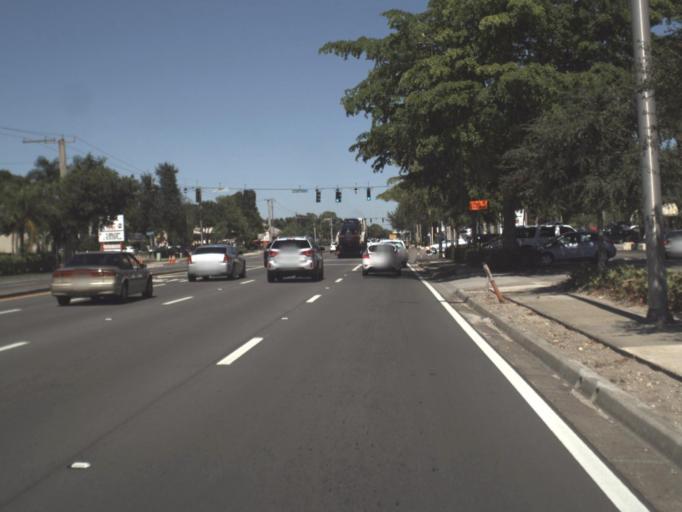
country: US
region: Florida
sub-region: Collier County
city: Naples
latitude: 26.1652
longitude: -81.7669
